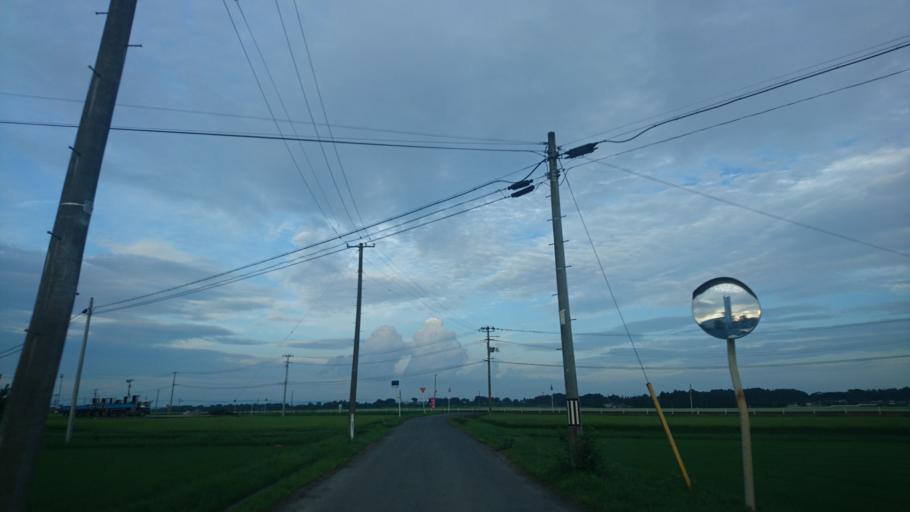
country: JP
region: Iwate
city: Ichinoseki
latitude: 38.7521
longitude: 141.0305
